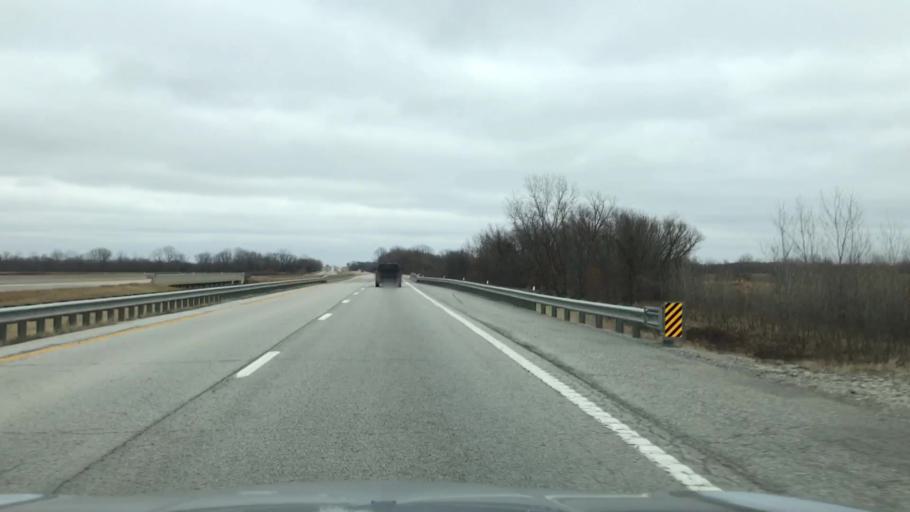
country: US
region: Missouri
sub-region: Livingston County
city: Chillicothe
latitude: 39.7767
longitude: -93.4358
